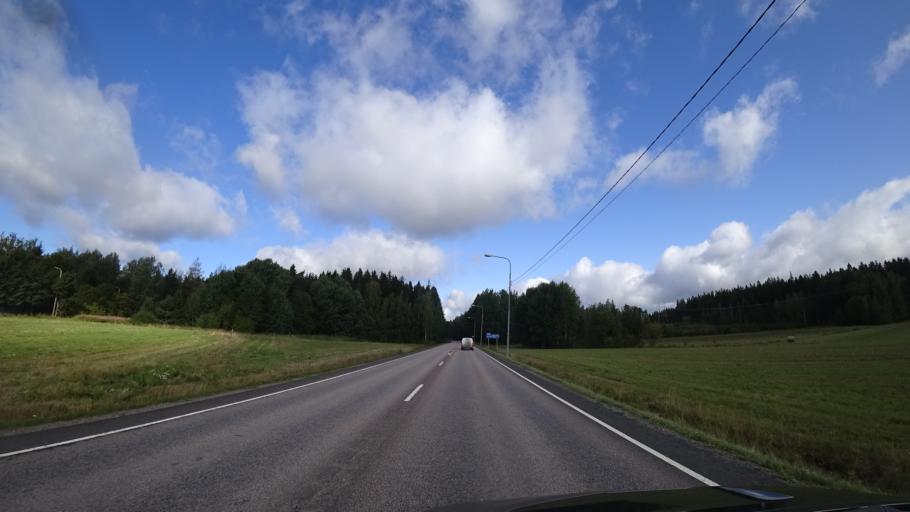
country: FI
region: Uusimaa
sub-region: Helsinki
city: Hyvinge
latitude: 60.5296
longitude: 24.9220
